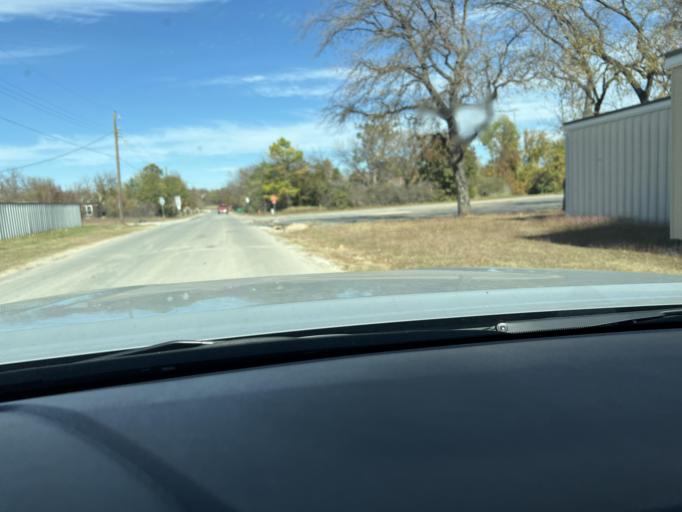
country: US
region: Texas
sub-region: Eastland County
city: Eastland
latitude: 32.3989
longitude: -98.8307
